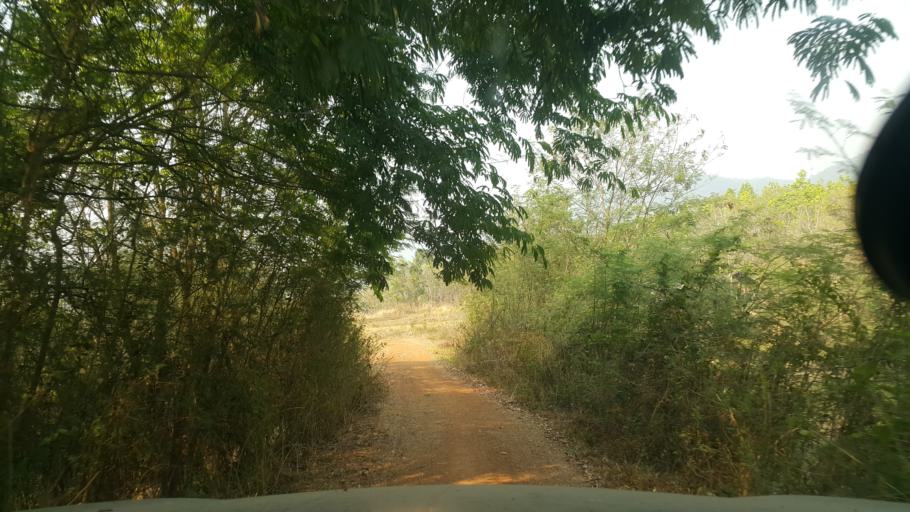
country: TH
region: Chiang Mai
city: Mae On
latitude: 18.7623
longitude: 99.2714
